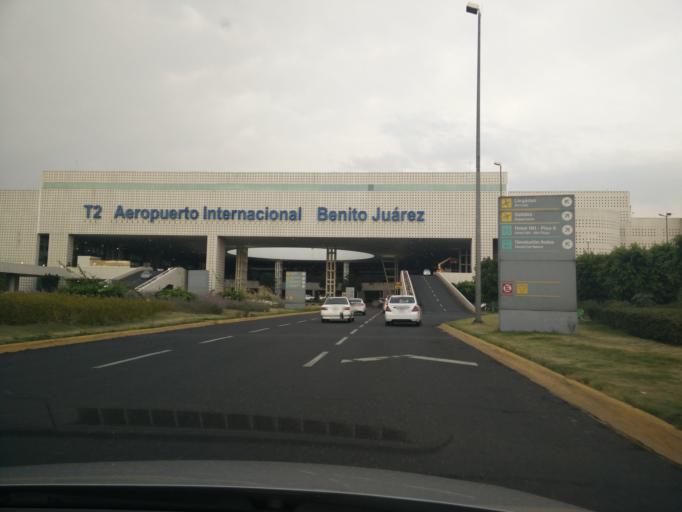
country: MX
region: Mexico City
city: Venustiano Carranza
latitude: 19.4193
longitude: -99.0781
